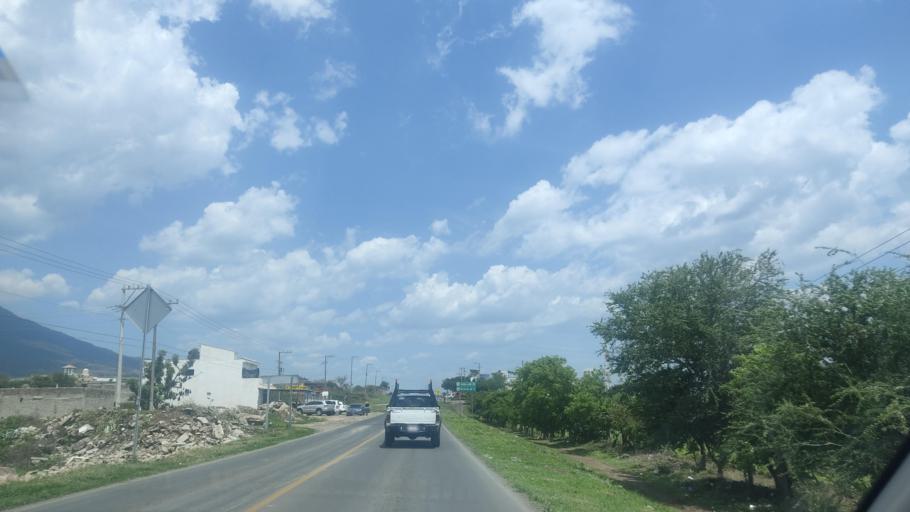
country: MX
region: Nayarit
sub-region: Tepic
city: La Corregidora
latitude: 21.4470
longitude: -104.8118
